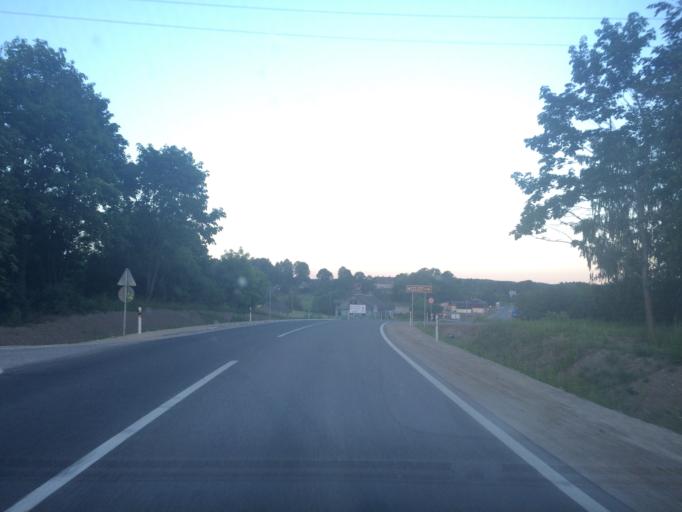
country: LT
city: Zarasai
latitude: 55.7464
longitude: 26.3130
